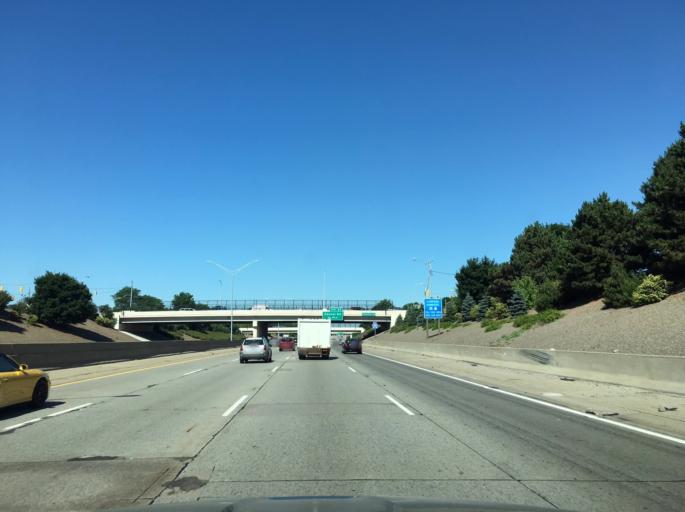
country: US
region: Michigan
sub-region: Macomb County
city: Eastpointe
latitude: 42.4928
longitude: -82.9854
